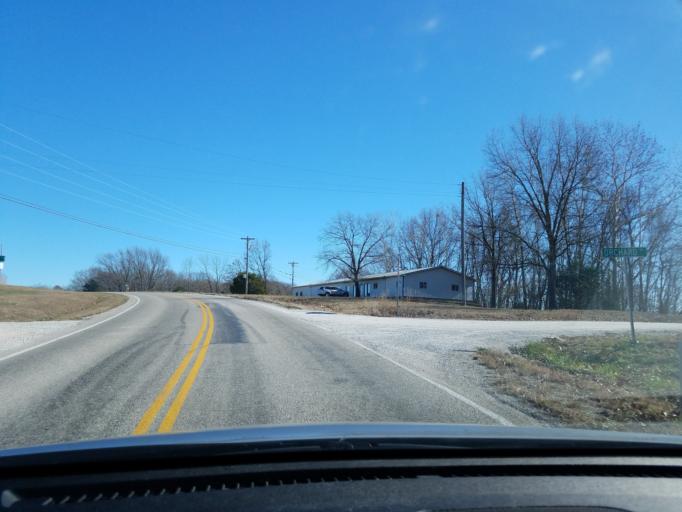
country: US
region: Missouri
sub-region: Taney County
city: Hollister
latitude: 36.5249
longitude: -93.2850
